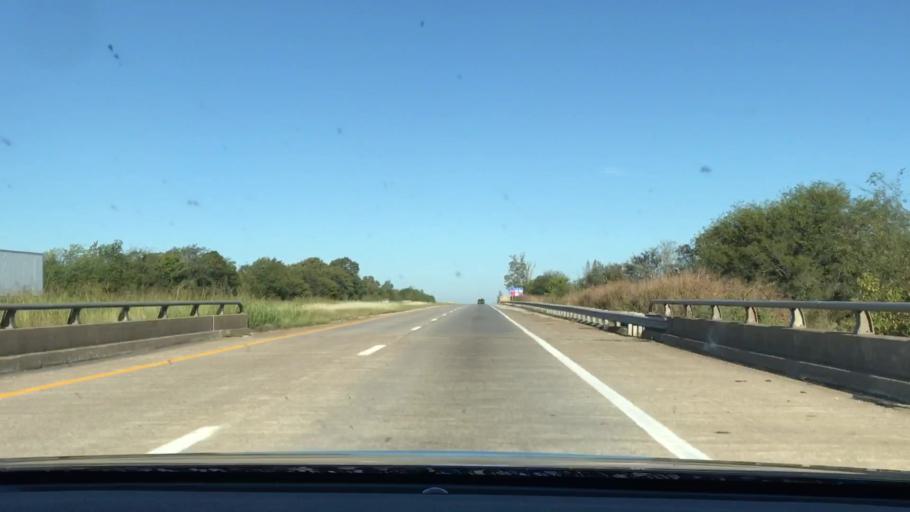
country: US
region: Kentucky
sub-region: Trigg County
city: Cadiz
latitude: 36.8721
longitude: -87.7177
